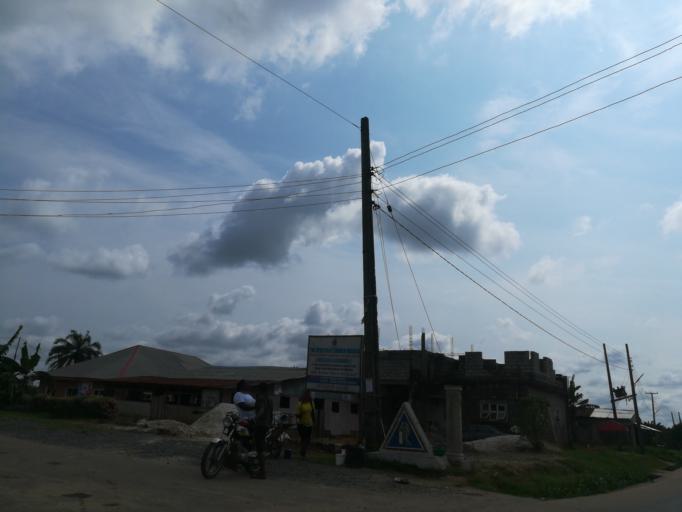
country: NG
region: Rivers
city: Okrika
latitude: 4.7412
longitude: 7.1170
